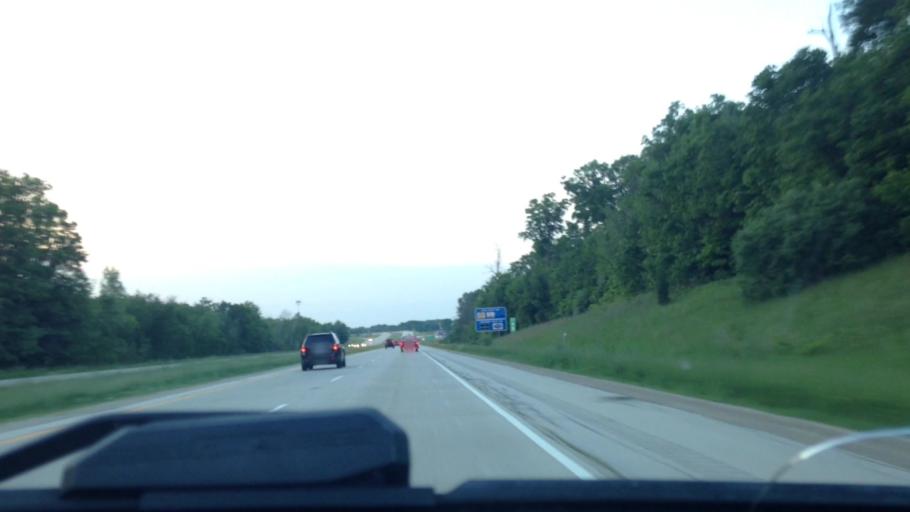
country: US
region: Wisconsin
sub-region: Washington County
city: West Bend
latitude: 43.3866
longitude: -88.1923
